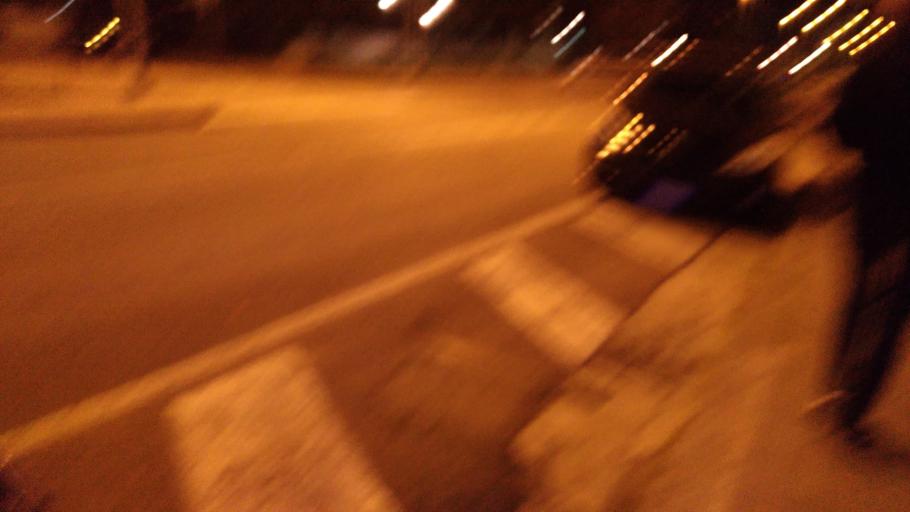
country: IT
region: Sardinia
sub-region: Provincia di Cagliari
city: Su Planu
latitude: 39.2409
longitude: 9.1029
